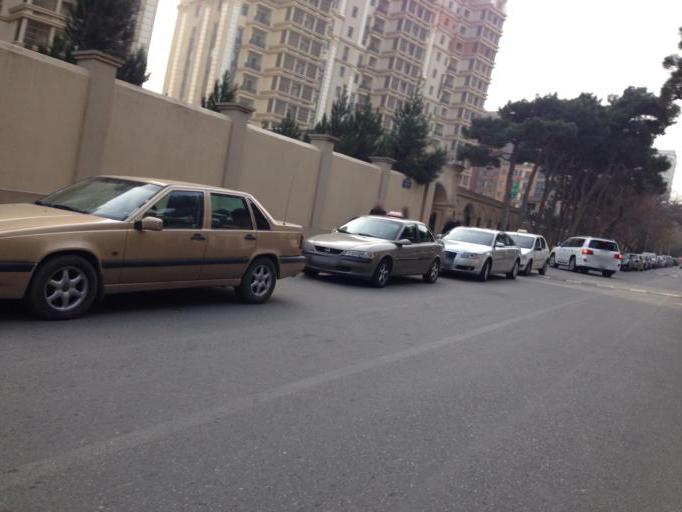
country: AZ
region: Baki
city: Baku
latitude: 40.4012
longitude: 49.8630
